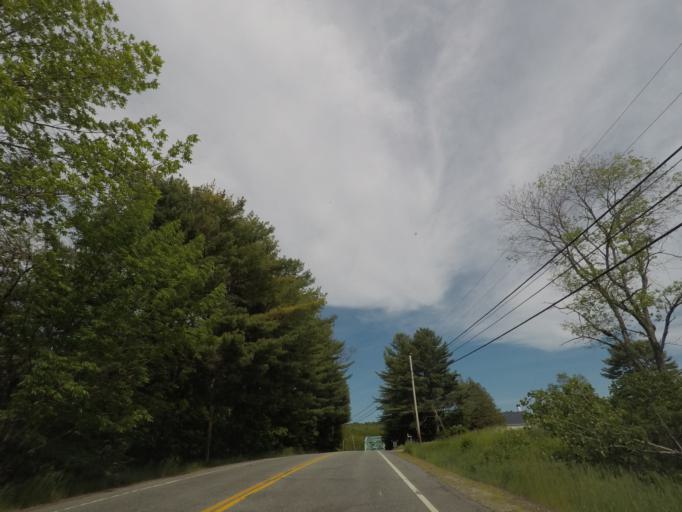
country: US
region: Maine
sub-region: Sagadahoc County
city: Richmond
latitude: 44.0844
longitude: -69.7506
